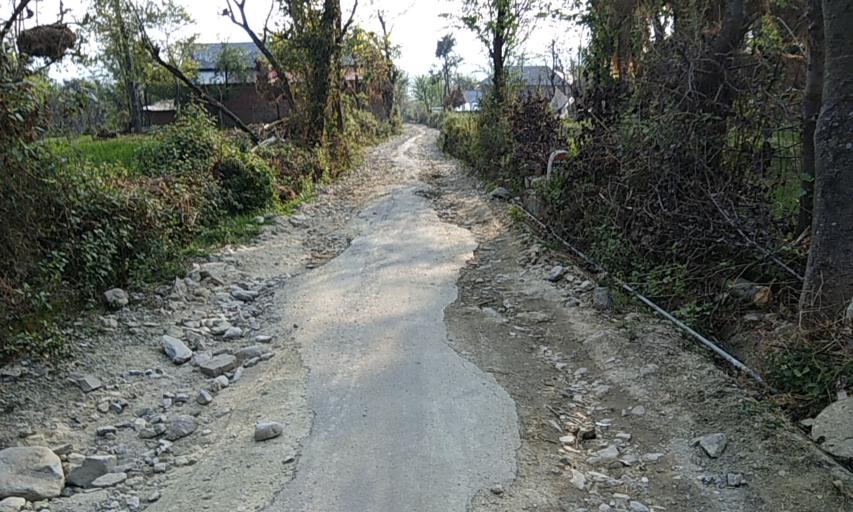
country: IN
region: Himachal Pradesh
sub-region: Kangra
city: Palampur
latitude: 32.1175
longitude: 76.5825
